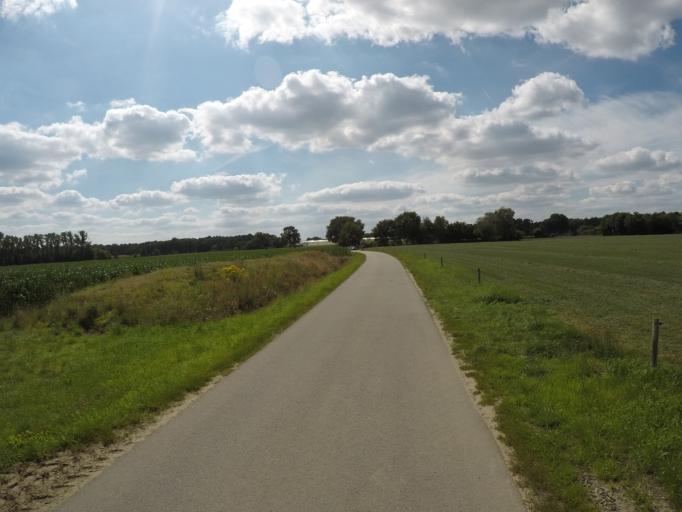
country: BE
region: Flanders
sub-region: Provincie Antwerpen
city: Herenthout
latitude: 51.1344
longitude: 4.7387
